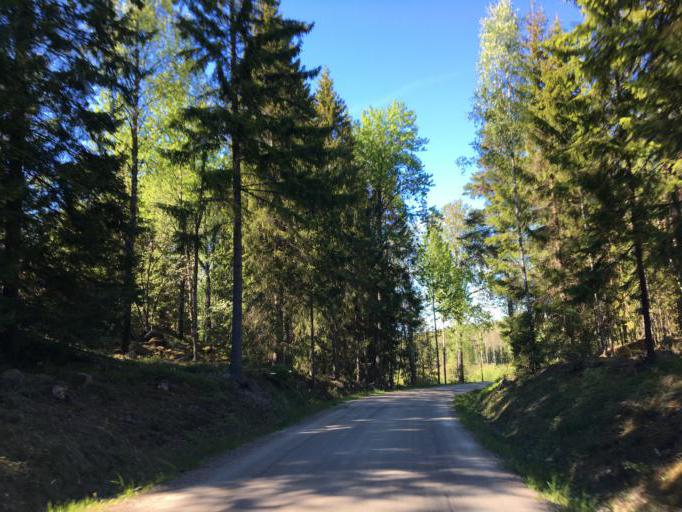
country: SE
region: Soedermanland
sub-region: Eskilstuna Kommun
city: Kvicksund
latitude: 59.3651
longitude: 16.2618
